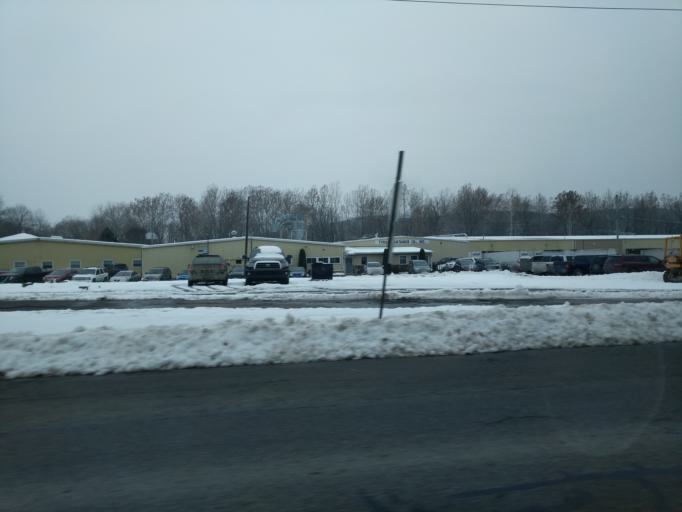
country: US
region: Pennsylvania
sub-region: Tioga County
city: Mansfield
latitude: 41.9116
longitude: -77.1332
